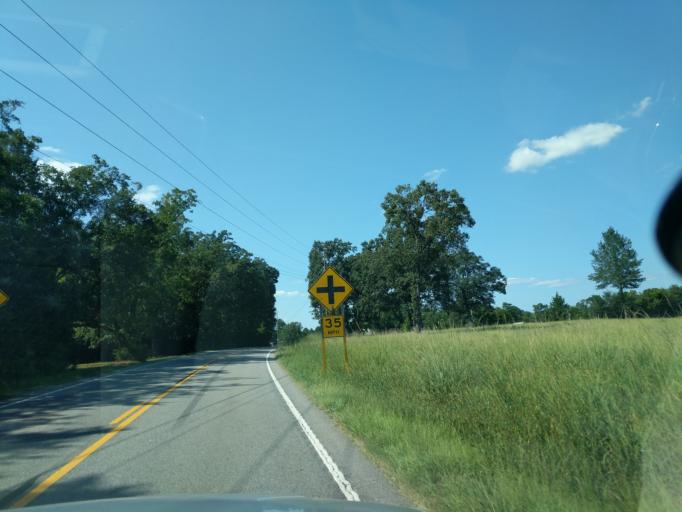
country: US
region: South Carolina
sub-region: Lexington County
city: Leesville
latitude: 34.0603
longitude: -81.5599
